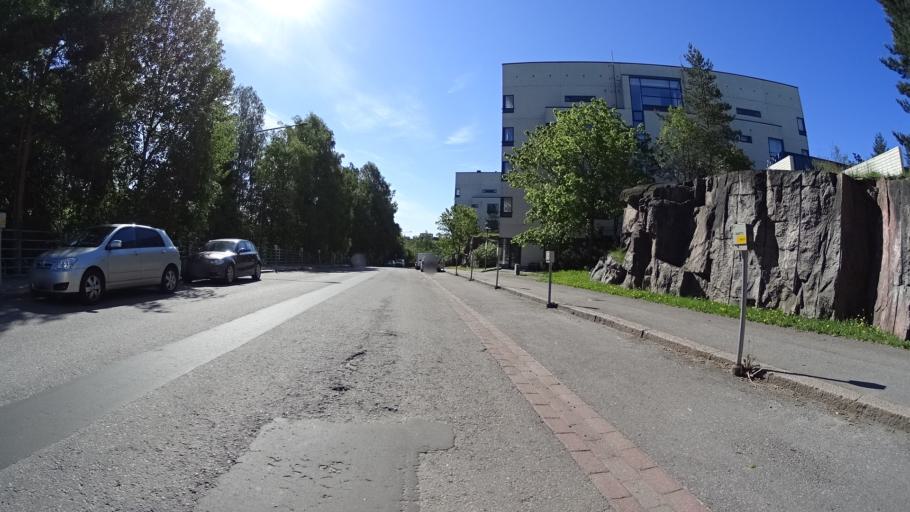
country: FI
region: Uusimaa
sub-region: Helsinki
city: Helsinki
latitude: 60.2136
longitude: 24.9674
